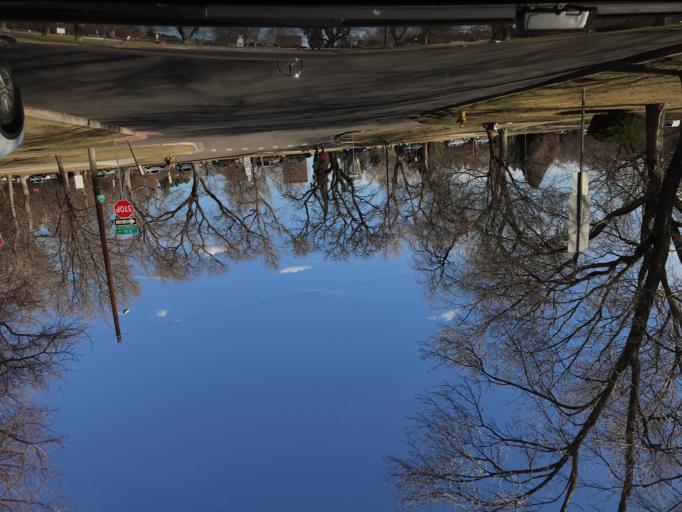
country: US
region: Colorado
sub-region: Denver County
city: Denver
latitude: 39.7287
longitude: -104.9659
